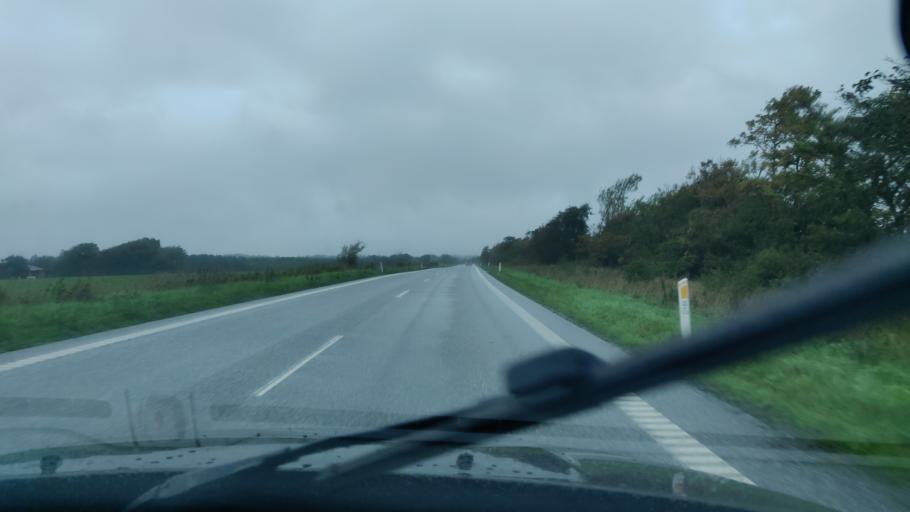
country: DK
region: North Denmark
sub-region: Thisted Kommune
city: Hurup
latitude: 56.8244
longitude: 8.4979
